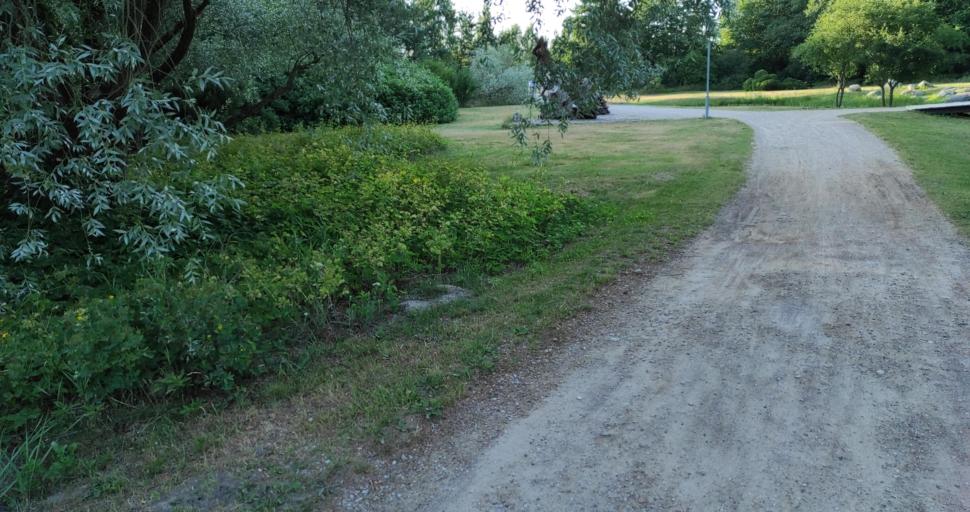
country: LV
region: Ventspils
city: Ventspils
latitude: 57.3861
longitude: 21.5300
